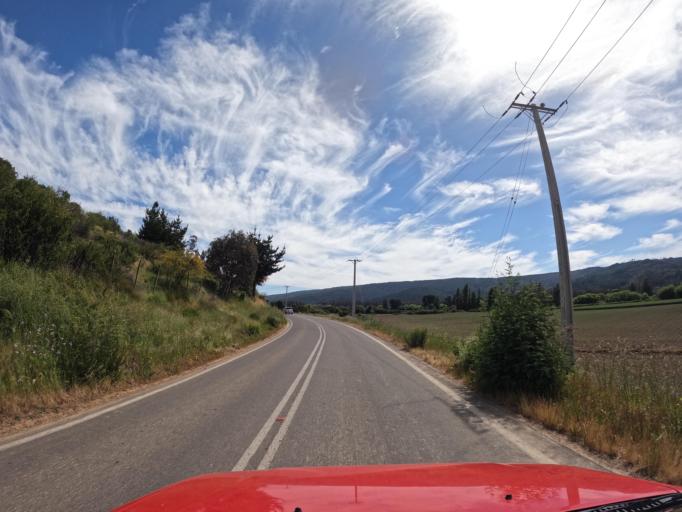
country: CL
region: Maule
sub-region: Provincia de Talca
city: Constitucion
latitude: -34.9945
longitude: -72.0186
